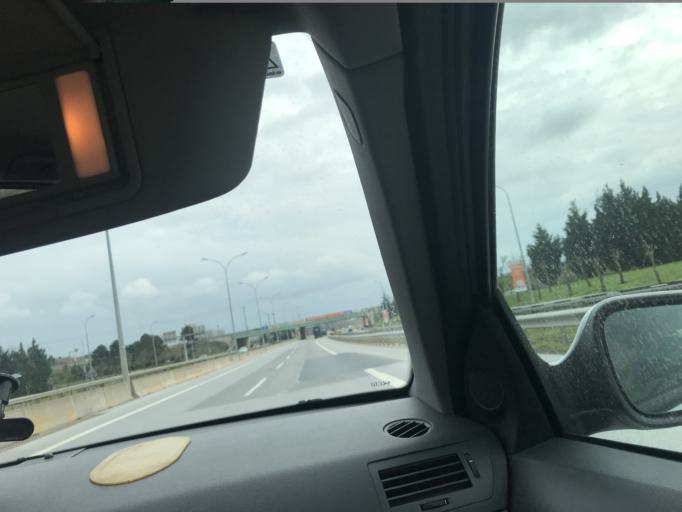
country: TR
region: Istanbul
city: Pendik
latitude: 40.9167
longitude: 29.3223
